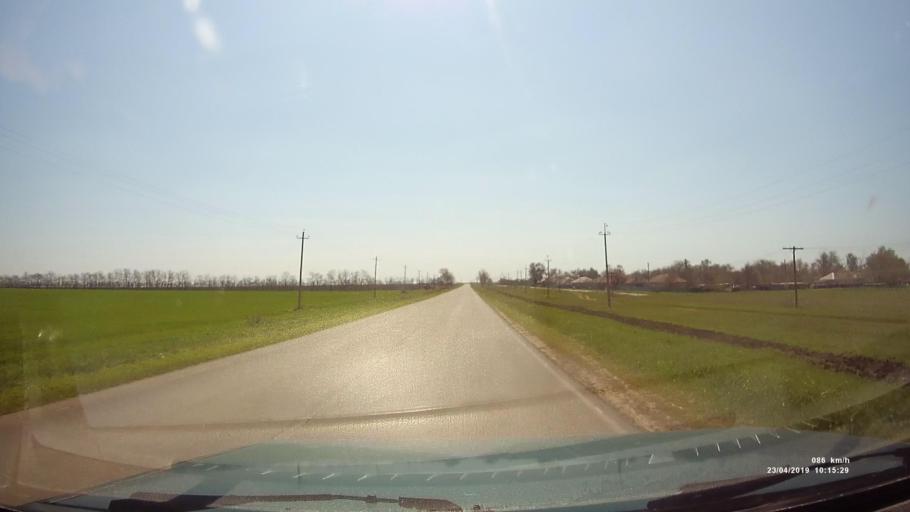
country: RU
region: Rostov
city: Sovetskoye
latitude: 46.6668
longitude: 42.3821
